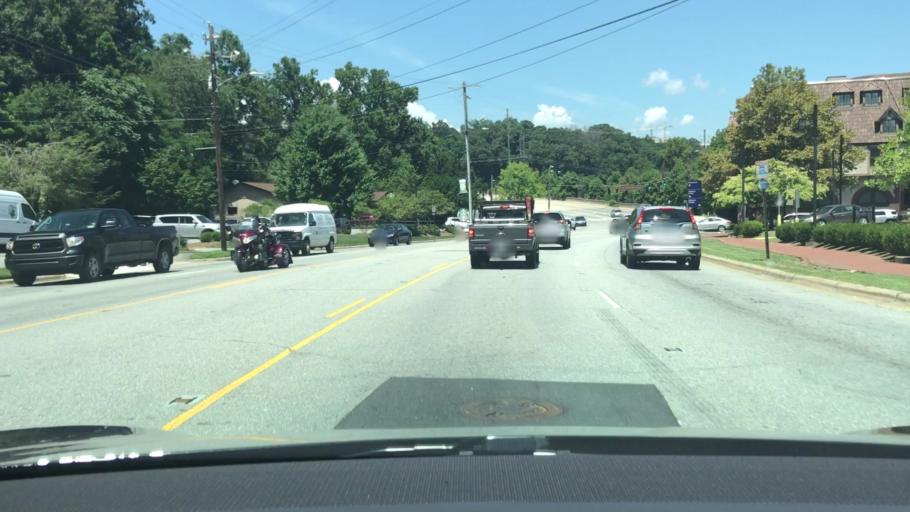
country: US
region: North Carolina
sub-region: Buncombe County
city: Biltmore Forest
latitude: 35.5658
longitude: -82.5439
